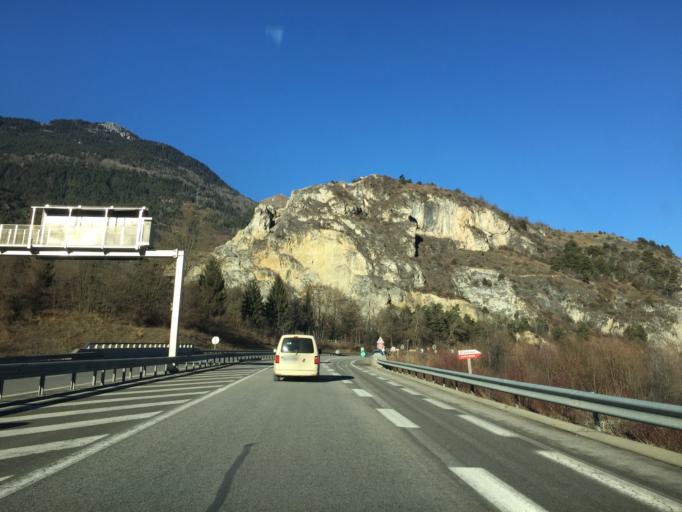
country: FR
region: Rhone-Alpes
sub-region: Departement de la Savoie
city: Aime
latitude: 45.5387
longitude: 6.6038
